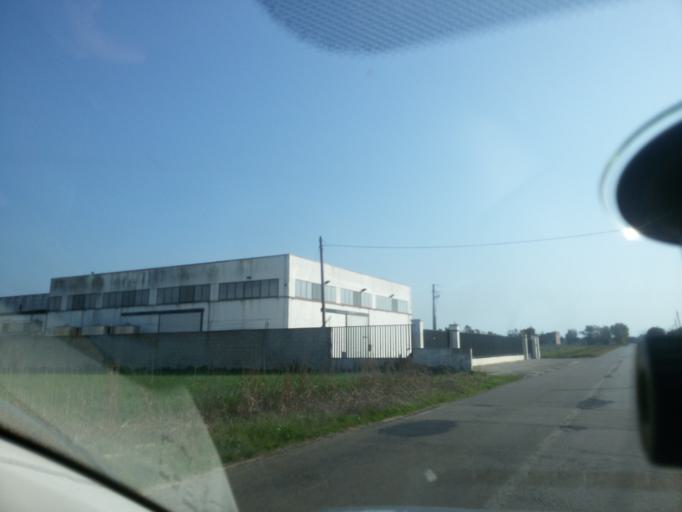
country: IT
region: Apulia
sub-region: Provincia di Brindisi
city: Mesagne
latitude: 40.5810
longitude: 17.8126
